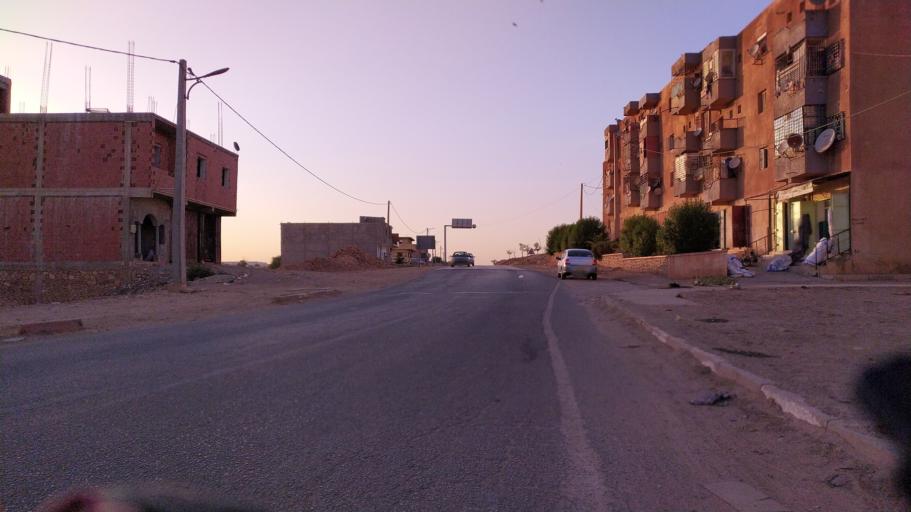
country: DZ
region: Tiaret
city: Frenda
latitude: 34.8976
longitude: 1.2476
